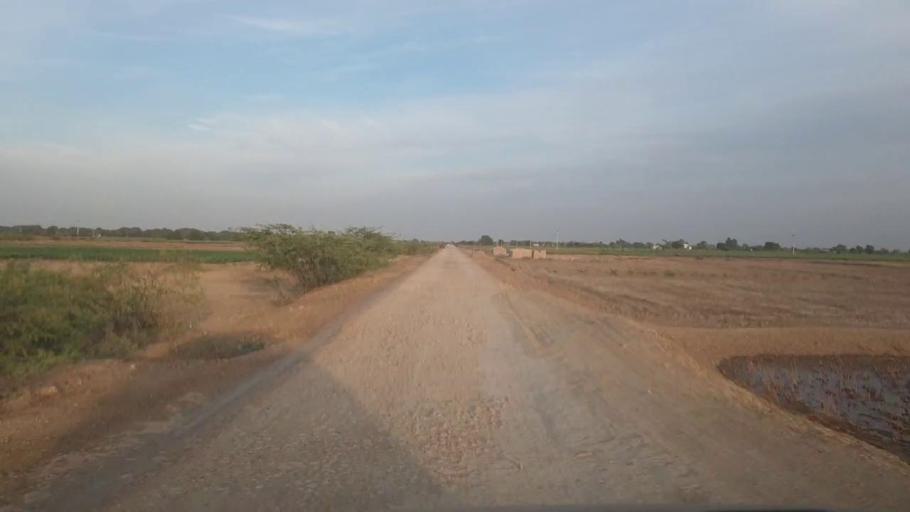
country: PK
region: Sindh
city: Kunri
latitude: 25.2269
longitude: 69.5578
